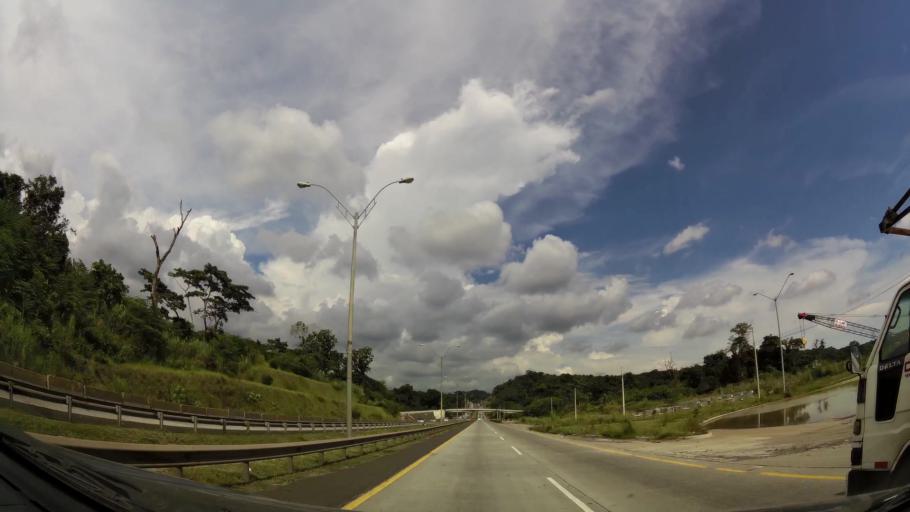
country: PA
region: Panama
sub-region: Distrito de Panama
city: Paraiso
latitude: 9.0335
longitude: -79.5803
